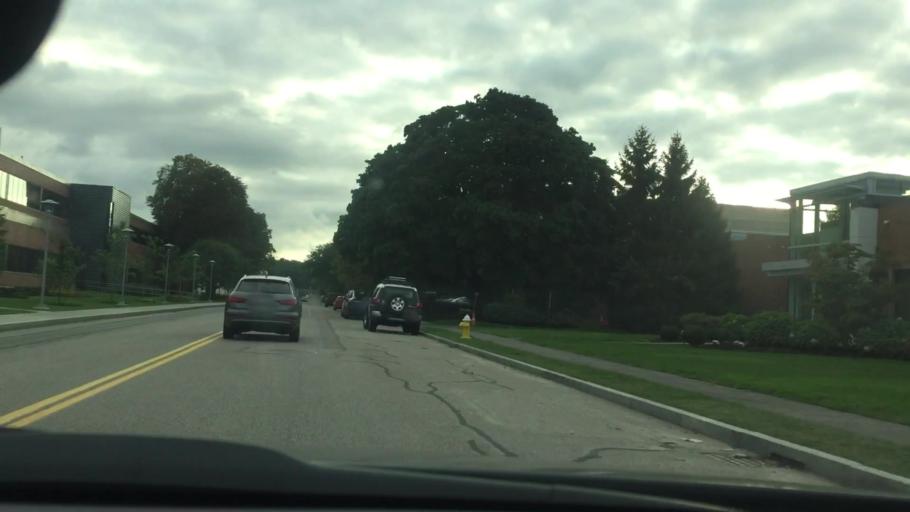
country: US
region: Massachusetts
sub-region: Norfolk County
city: Needham
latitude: 42.3018
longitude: -71.2169
